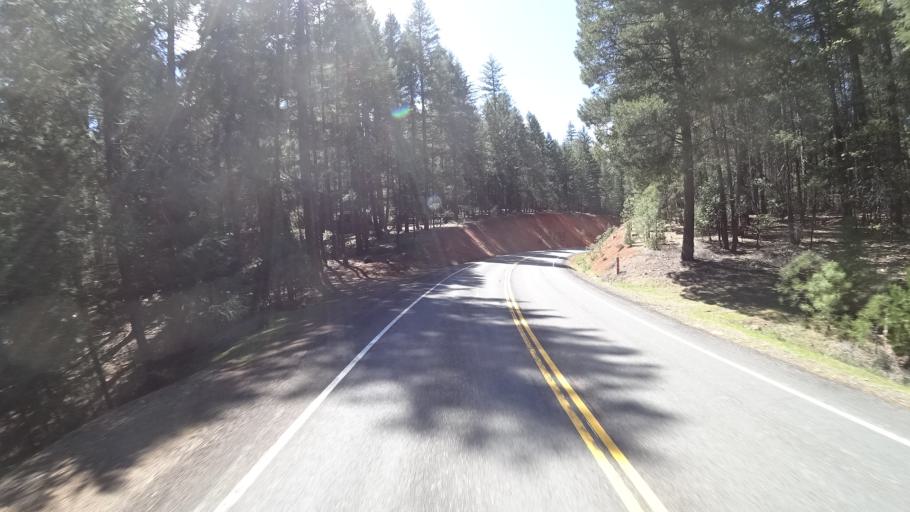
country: US
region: California
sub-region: Trinity County
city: Lewiston
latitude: 40.8457
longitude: -122.8447
